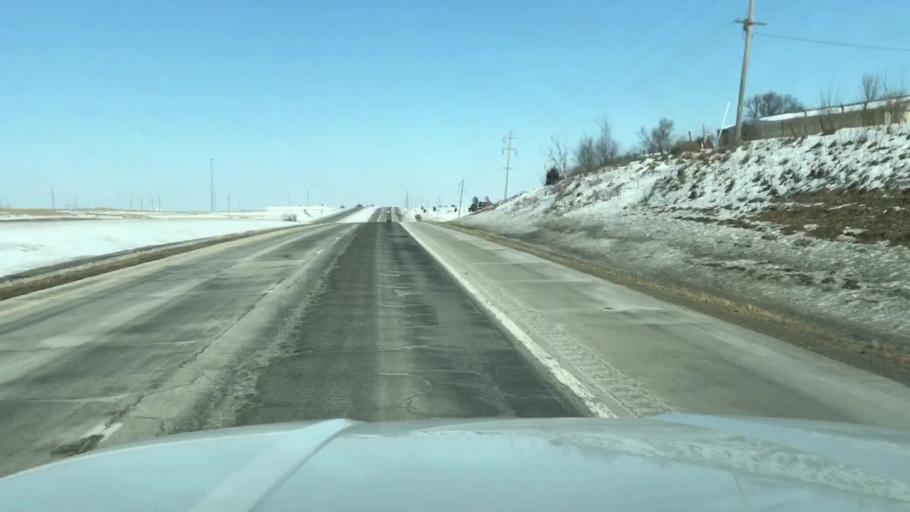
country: US
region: Missouri
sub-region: Nodaway County
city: Maryville
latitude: 40.2185
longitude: -94.8679
